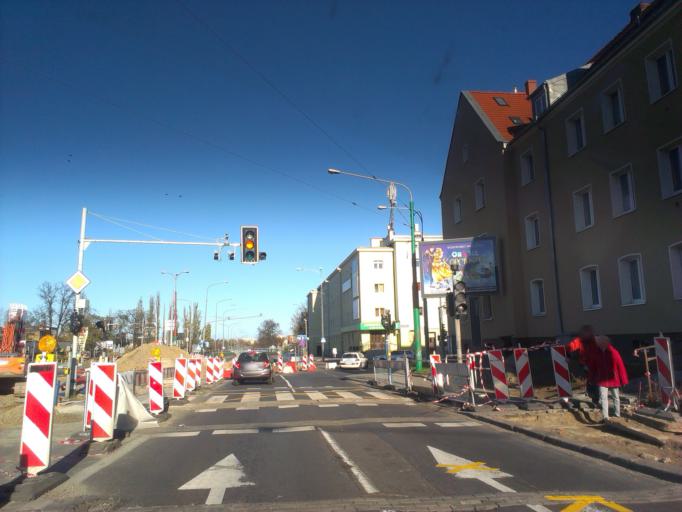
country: PL
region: Greater Poland Voivodeship
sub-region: Poznan
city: Poznan
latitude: 52.4149
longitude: 16.8914
